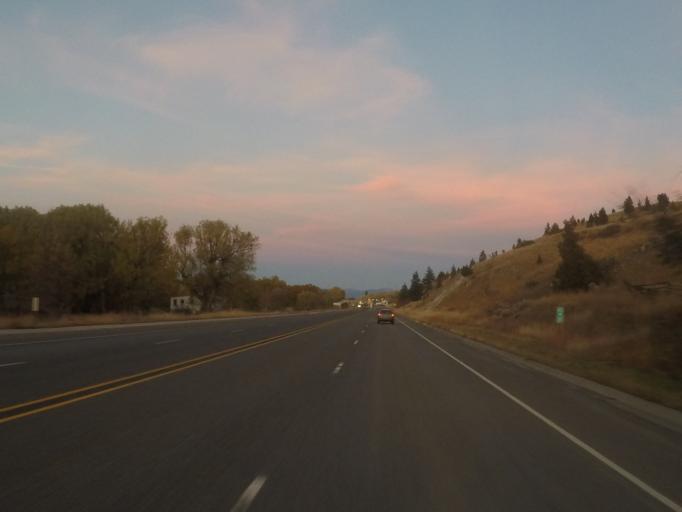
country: US
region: Montana
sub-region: Lewis and Clark County
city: Helena West Side
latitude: 46.6009
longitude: -112.0947
